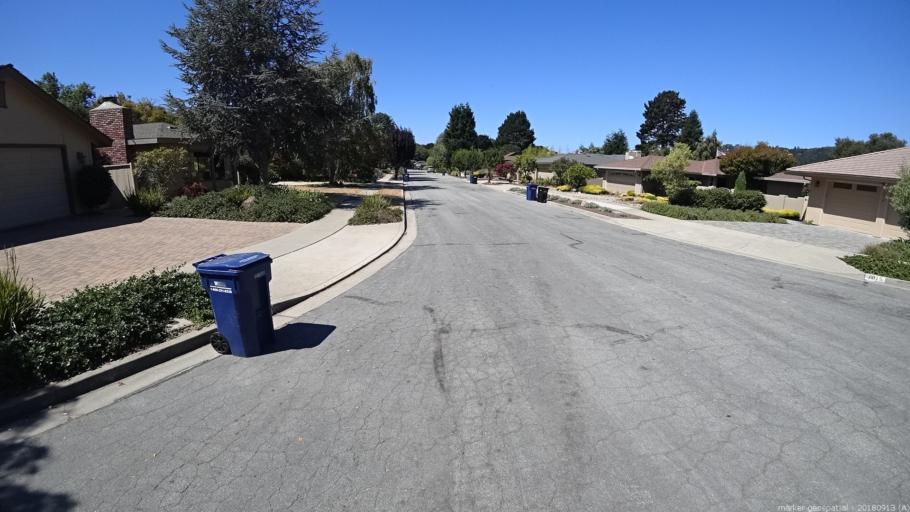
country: US
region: California
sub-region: Monterey County
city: Carmel-by-the-Sea
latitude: 36.5317
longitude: -121.8663
